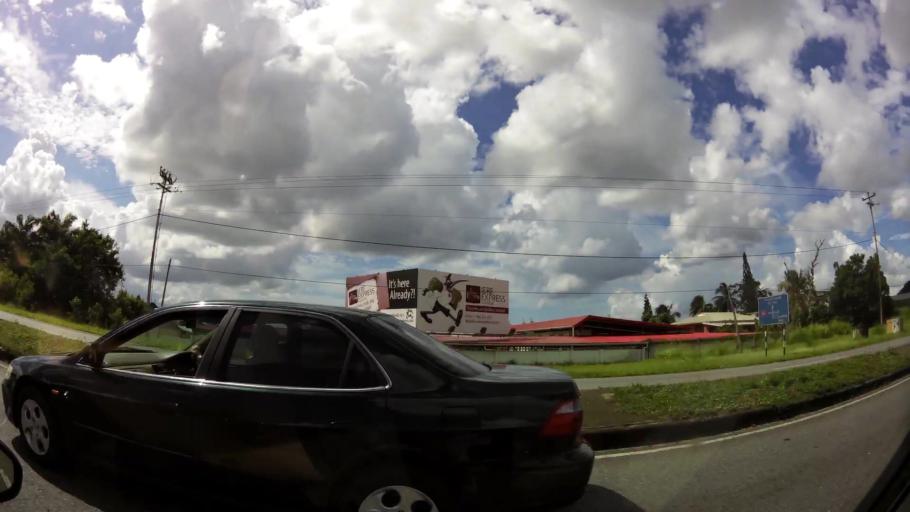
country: TT
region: City of San Fernando
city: Mon Repos
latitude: 10.2656
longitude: -61.4567
